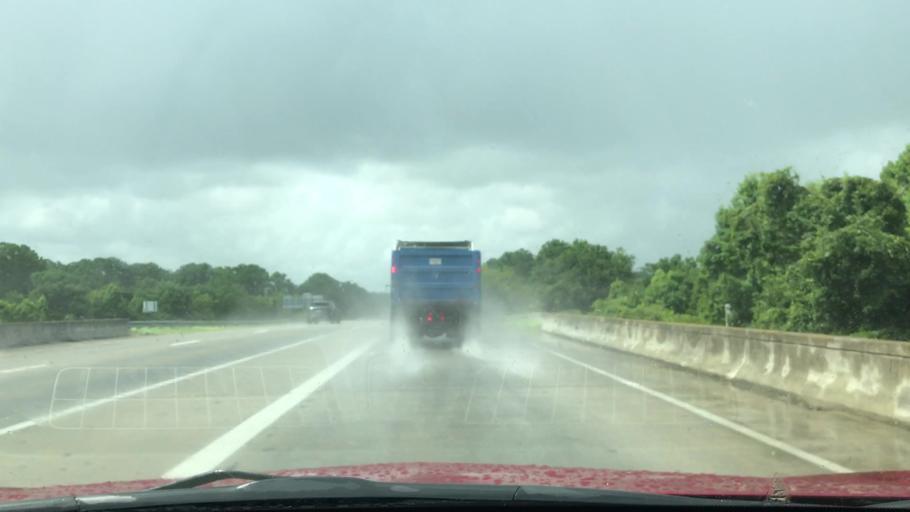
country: US
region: South Carolina
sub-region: Charleston County
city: Mount Pleasant
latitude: 32.8236
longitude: -79.8495
